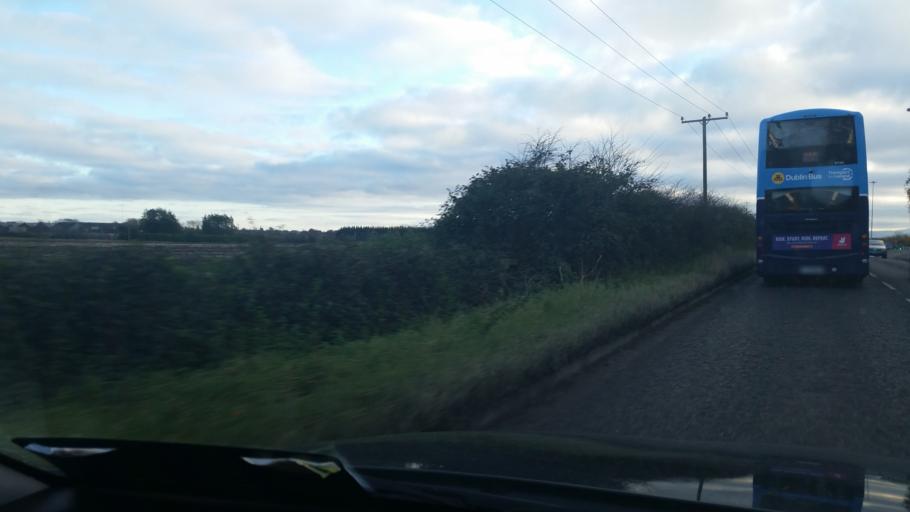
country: IE
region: Leinster
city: Ballymun
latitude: 53.4132
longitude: -6.2654
